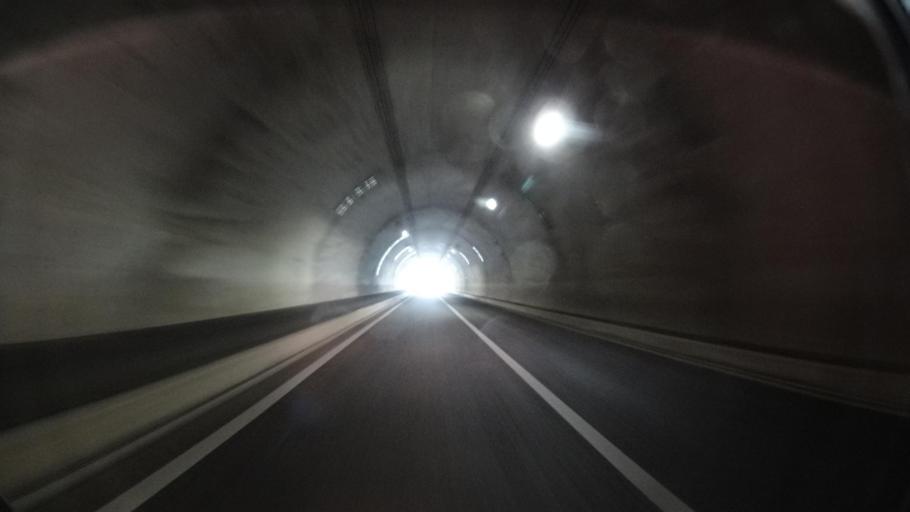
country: JP
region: Kyoto
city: Maizuru
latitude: 35.5342
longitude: 135.3474
